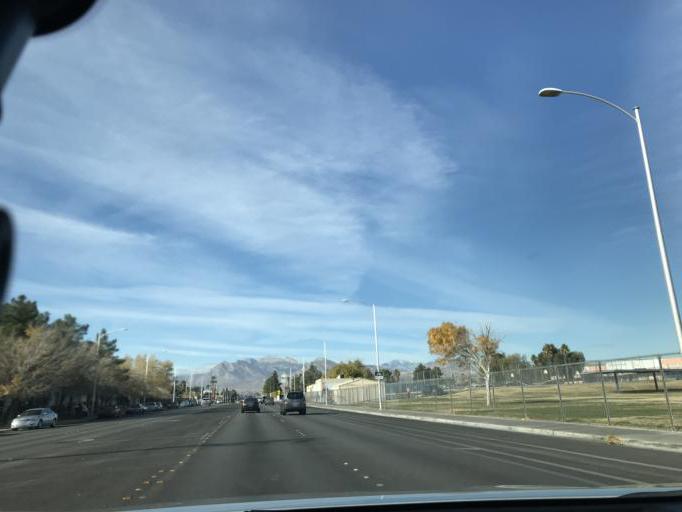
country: US
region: Nevada
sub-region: Clark County
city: Las Vegas
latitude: 36.2031
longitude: -115.2256
